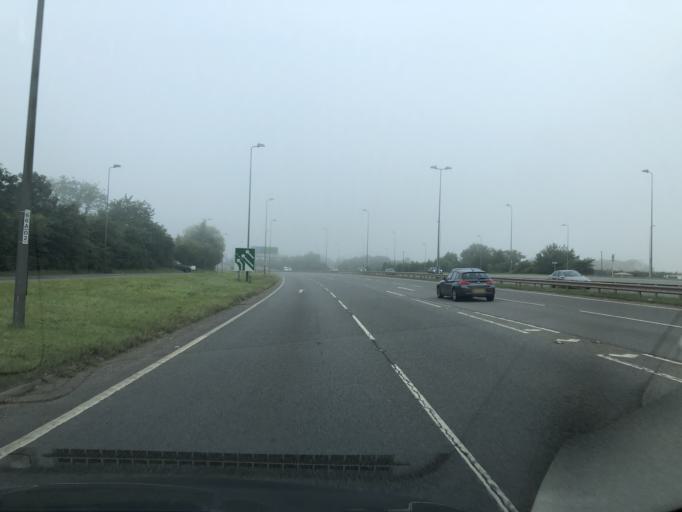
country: GB
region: England
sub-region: Solihull
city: Hampton in Arden
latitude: 52.4456
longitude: -1.6929
